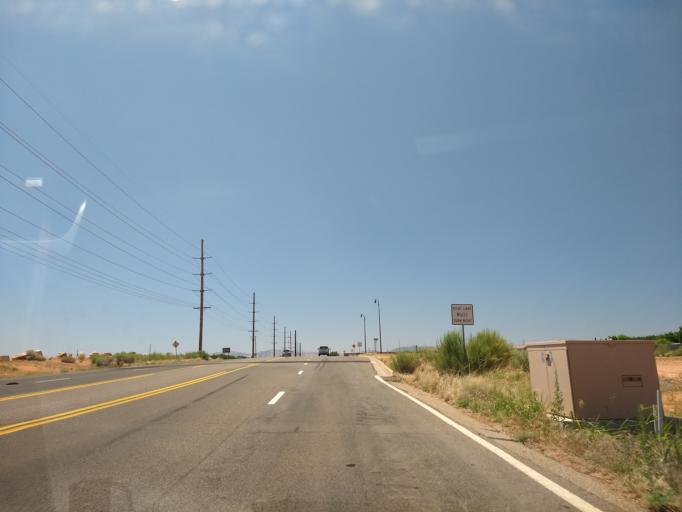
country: US
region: Utah
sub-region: Washington County
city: Washington
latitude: 37.1312
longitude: -113.4841
